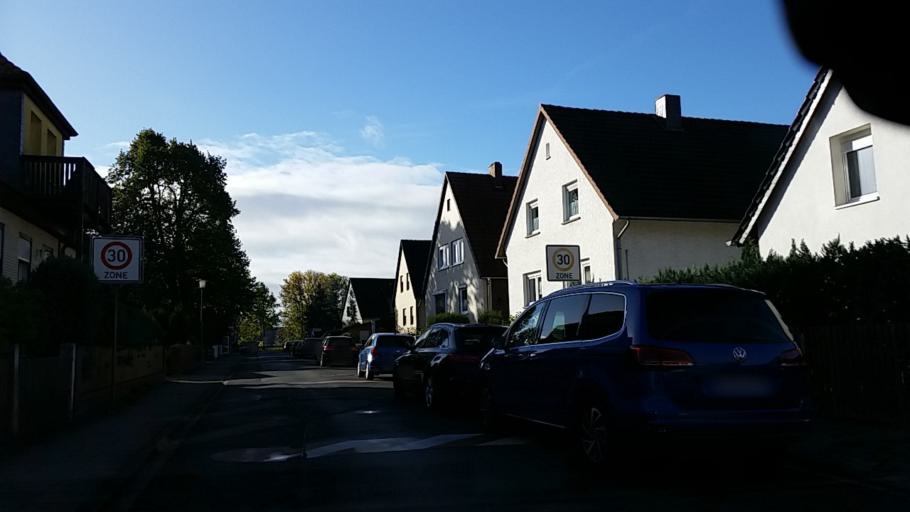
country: DE
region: Lower Saxony
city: Wolfsburg
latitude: 52.4284
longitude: 10.7551
